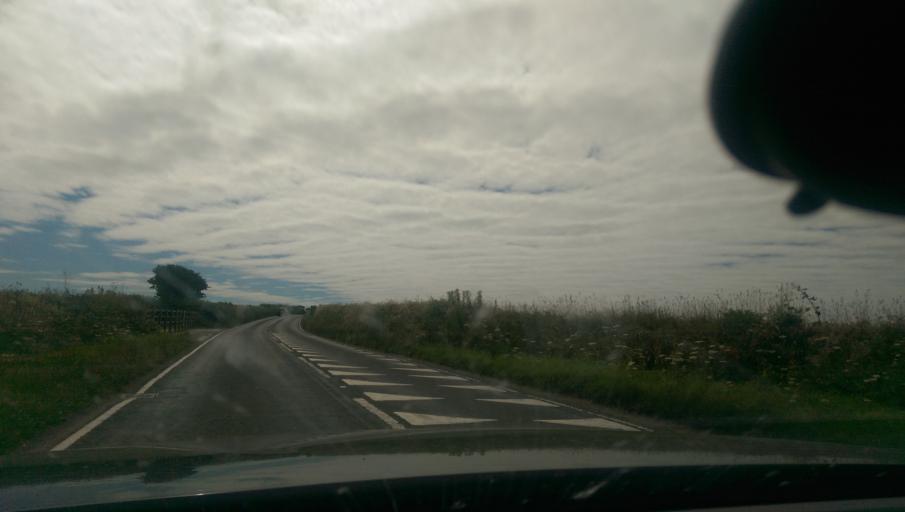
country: GB
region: England
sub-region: Cornwall
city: Wadebridge
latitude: 50.5118
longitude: -4.8737
